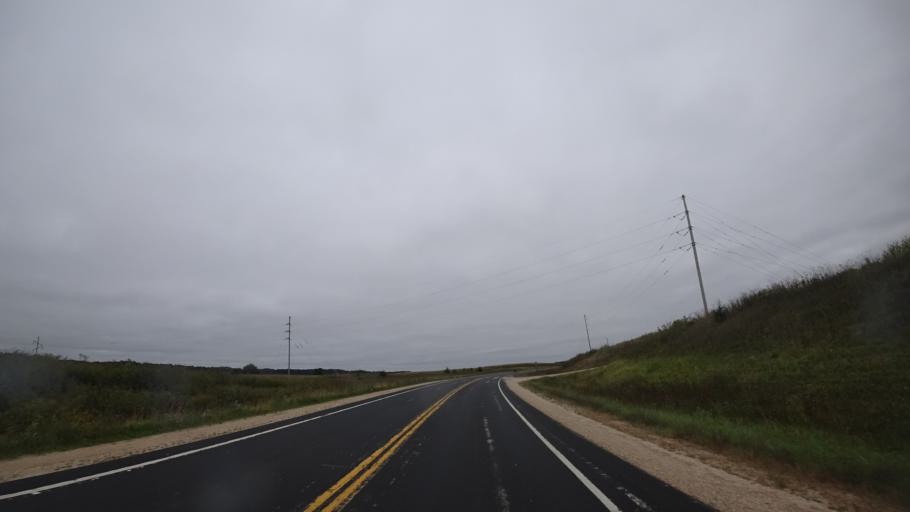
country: US
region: Wisconsin
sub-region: Grant County
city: Boscobel
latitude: 43.1062
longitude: -90.8102
